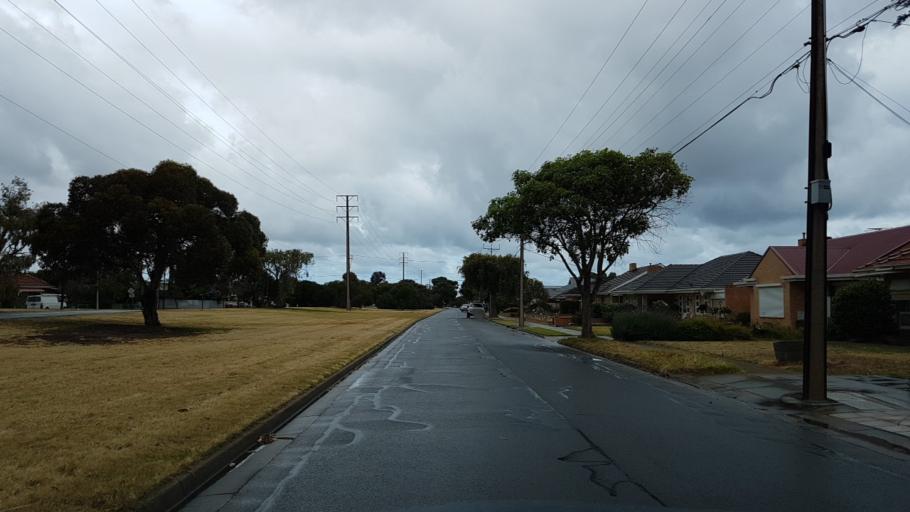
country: AU
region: South Australia
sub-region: City of West Torrens
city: Plympton
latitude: -34.9628
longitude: 138.5520
